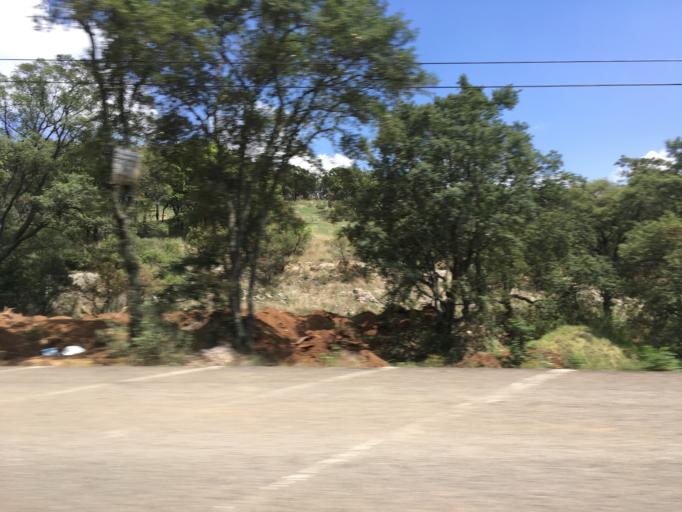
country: MX
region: Mexico
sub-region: Timilpan
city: Tercera Manzana de Zaragoza
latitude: 19.8657
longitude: -99.7091
